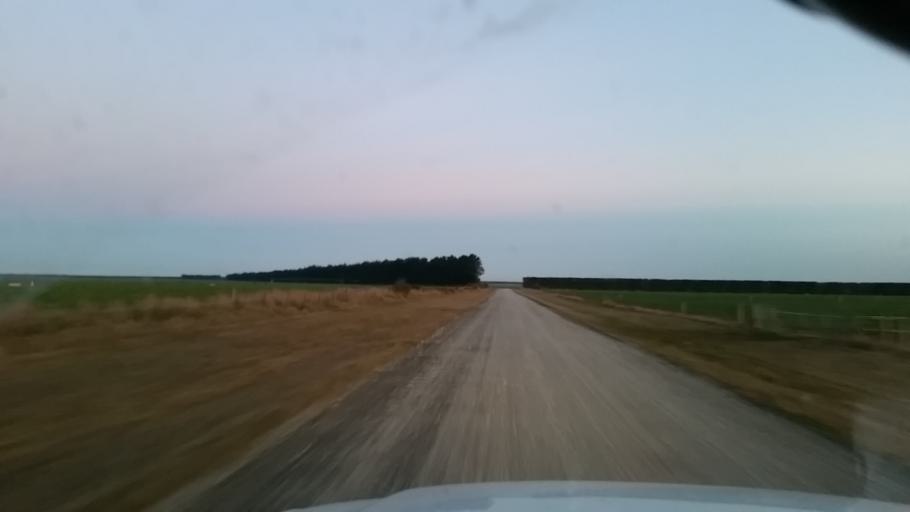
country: NZ
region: Canterbury
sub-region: Ashburton District
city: Tinwald
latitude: -43.9421
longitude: 171.6103
